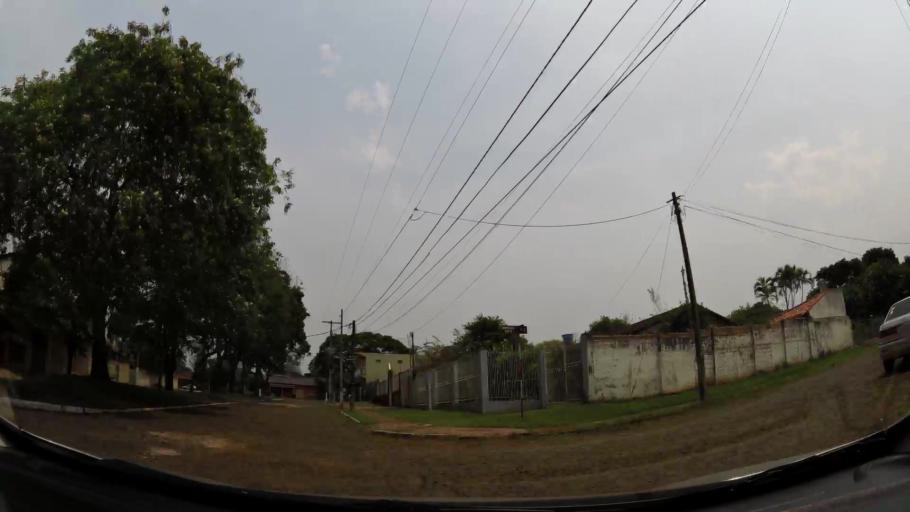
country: PY
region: Alto Parana
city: Presidente Franco
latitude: -25.5562
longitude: -54.6154
